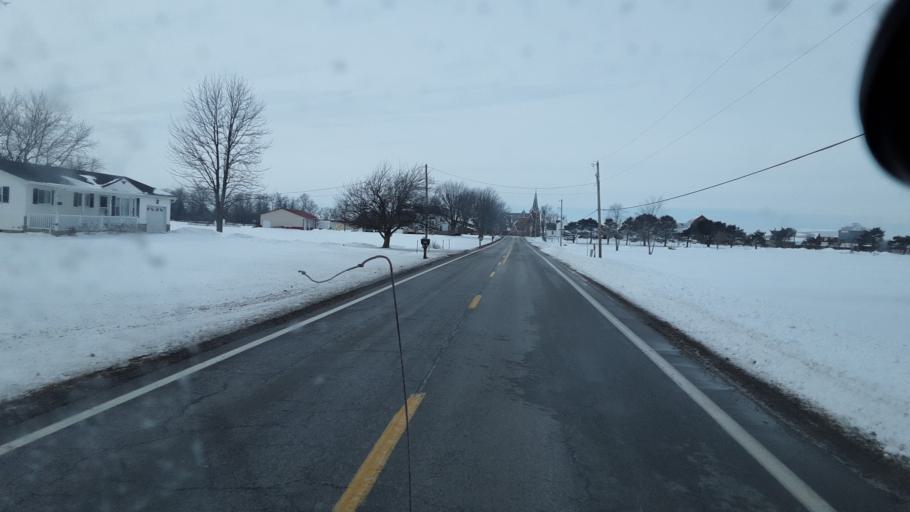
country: US
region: Ohio
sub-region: Union County
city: Marysville
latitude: 40.1862
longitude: -83.3470
